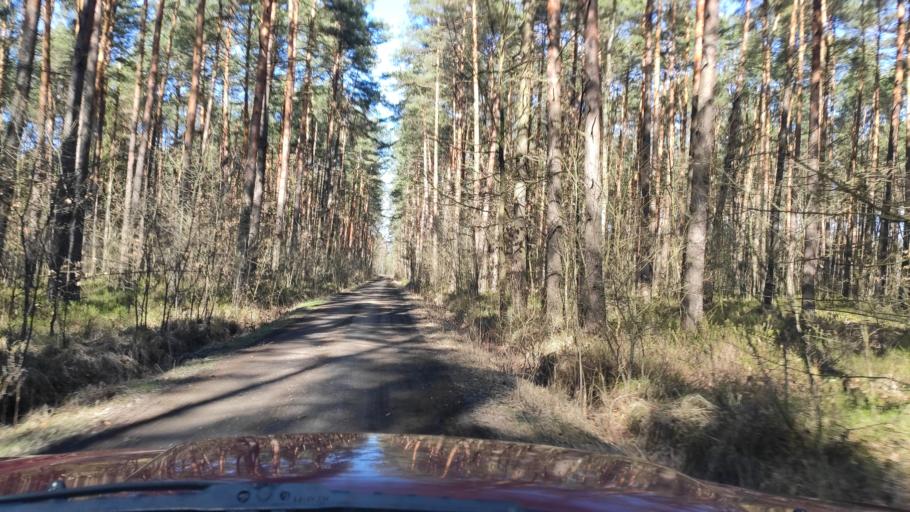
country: PL
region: Masovian Voivodeship
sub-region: Powiat kozienicki
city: Garbatka-Letnisko
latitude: 51.4382
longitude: 21.5439
